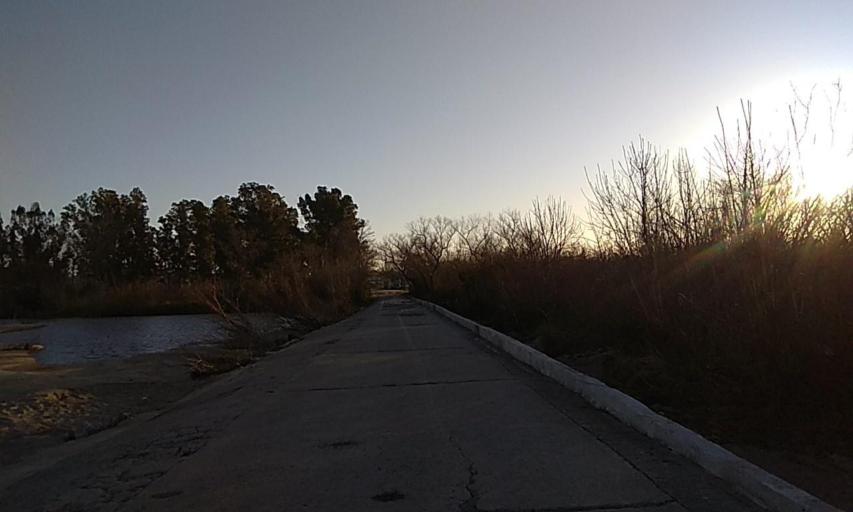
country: UY
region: Florida
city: Florida
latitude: -34.0918
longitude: -56.2049
